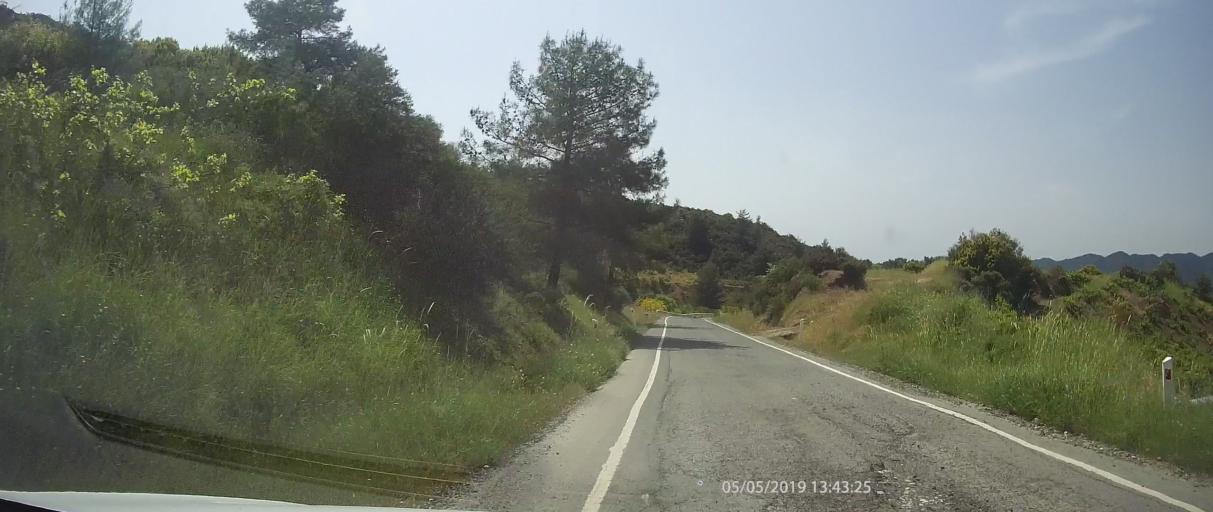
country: CY
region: Limassol
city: Pachna
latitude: 34.8731
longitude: 32.7976
